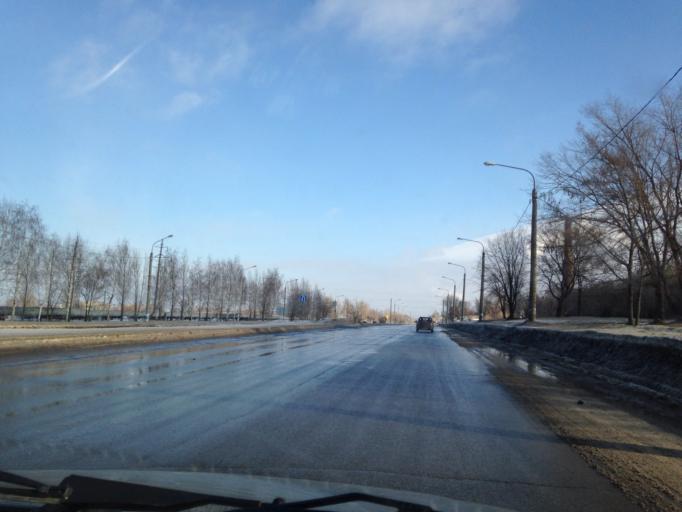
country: RU
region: Ulyanovsk
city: Mirnyy
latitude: 54.3479
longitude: 48.5750
